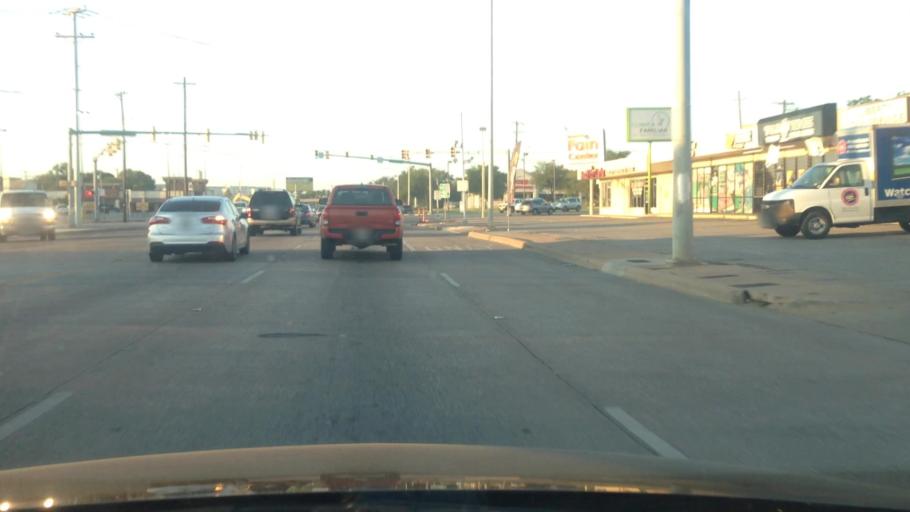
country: US
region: Texas
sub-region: Tarrant County
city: Haltom City
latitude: 32.7819
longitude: -97.2908
